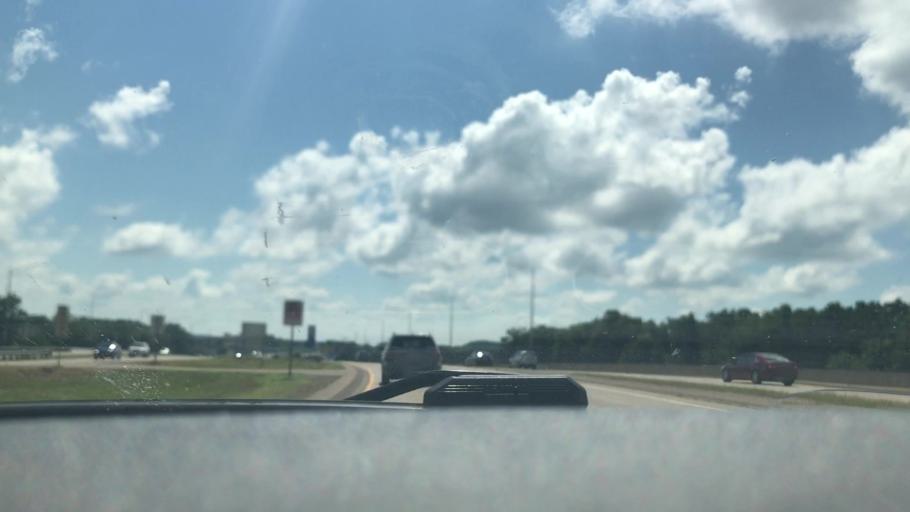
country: US
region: Wisconsin
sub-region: Eau Claire County
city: Altoona
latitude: 44.7854
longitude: -91.4507
